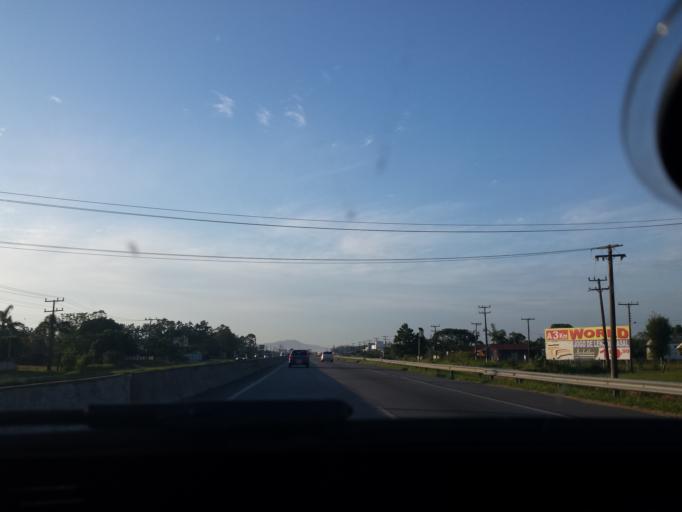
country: BR
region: Santa Catarina
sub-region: Imbituba
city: Imbituba
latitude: -28.1348
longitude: -48.6922
